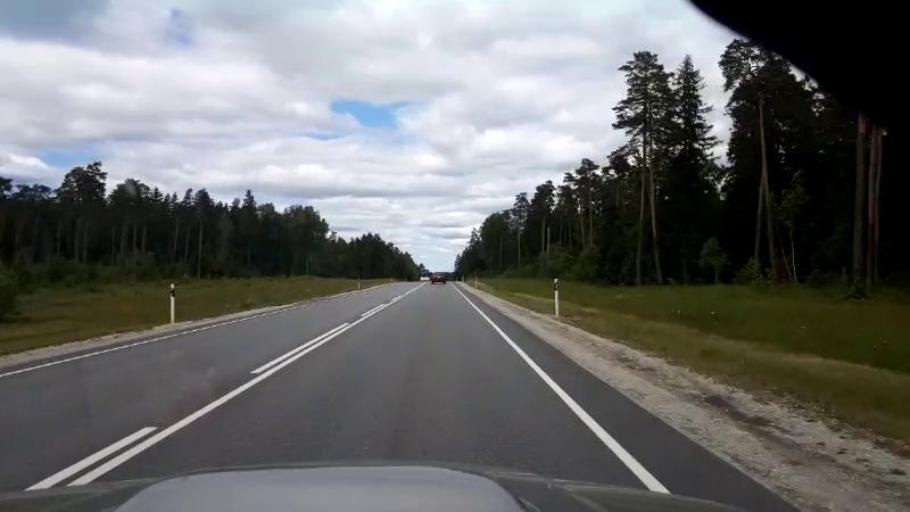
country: EE
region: Raplamaa
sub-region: Maerjamaa vald
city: Marjamaa
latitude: 58.9345
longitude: 24.4637
